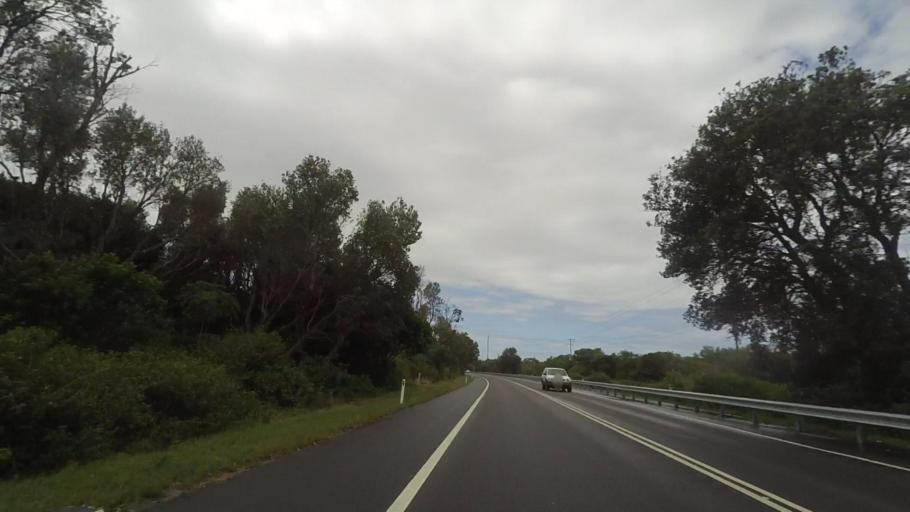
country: AU
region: New South Wales
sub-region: Wyong Shire
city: The Entrance
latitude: -33.3183
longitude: 151.5172
